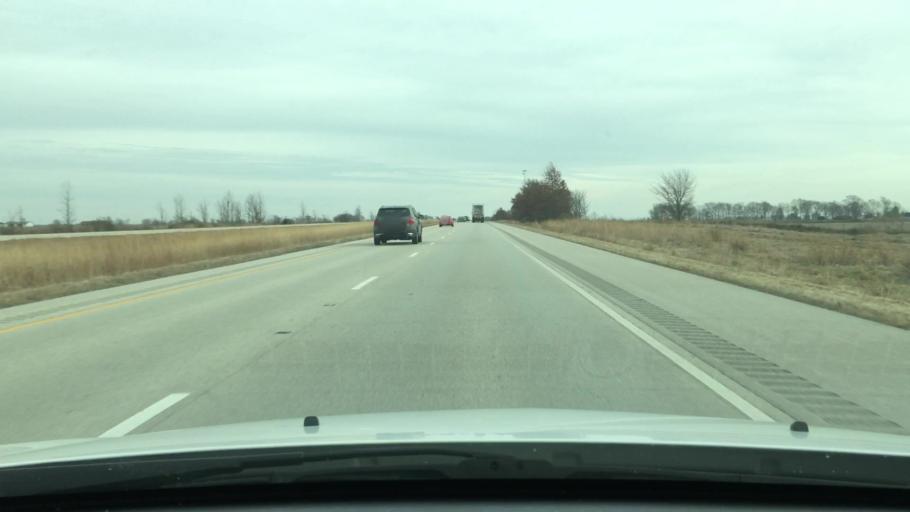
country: US
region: Illinois
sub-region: Sangamon County
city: New Berlin
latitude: 39.7404
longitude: -89.8836
